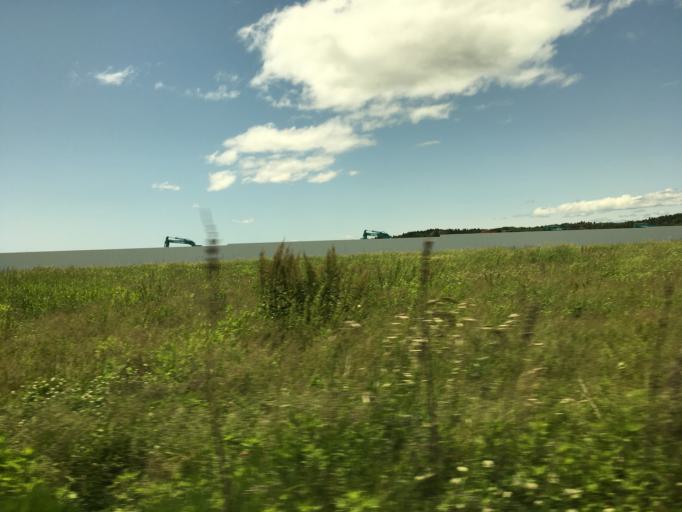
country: JP
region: Fukushima
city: Namie
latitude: 37.4804
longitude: 141.0318
